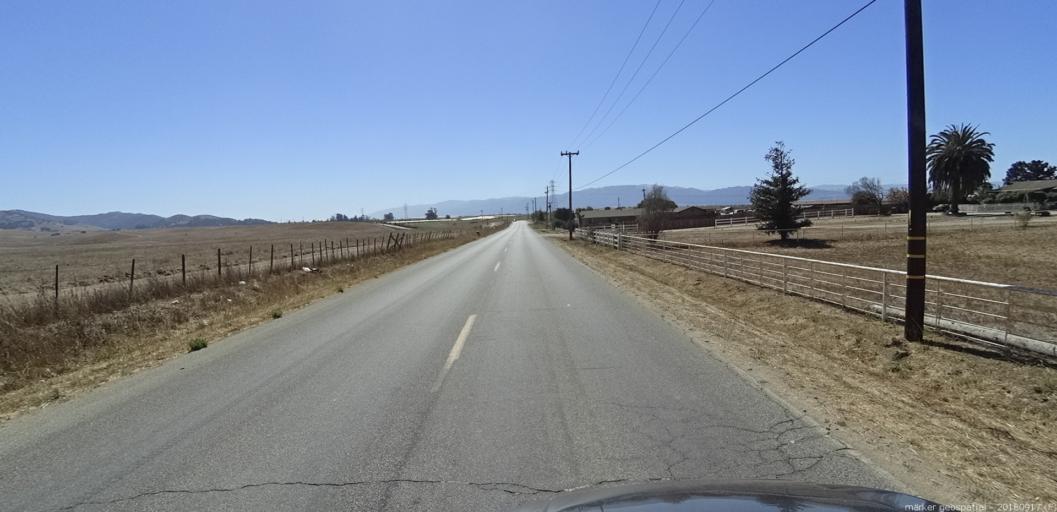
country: US
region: California
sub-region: Monterey County
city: Salinas
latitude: 36.7228
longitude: -121.5939
